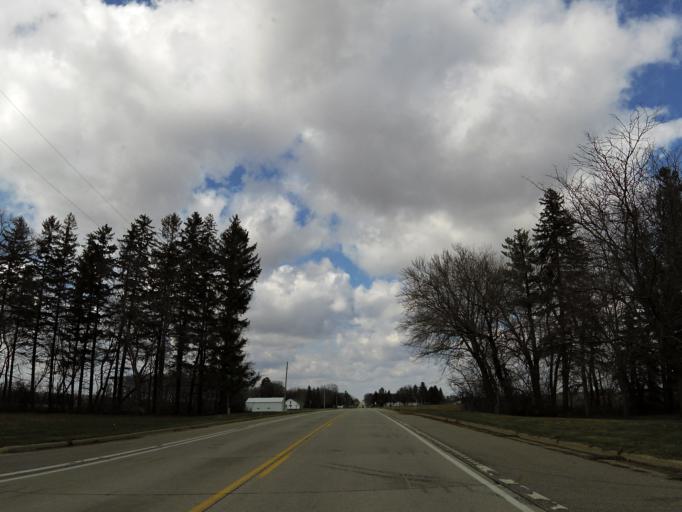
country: US
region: Minnesota
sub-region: Olmsted County
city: Byron
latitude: 44.0897
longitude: -92.6783
